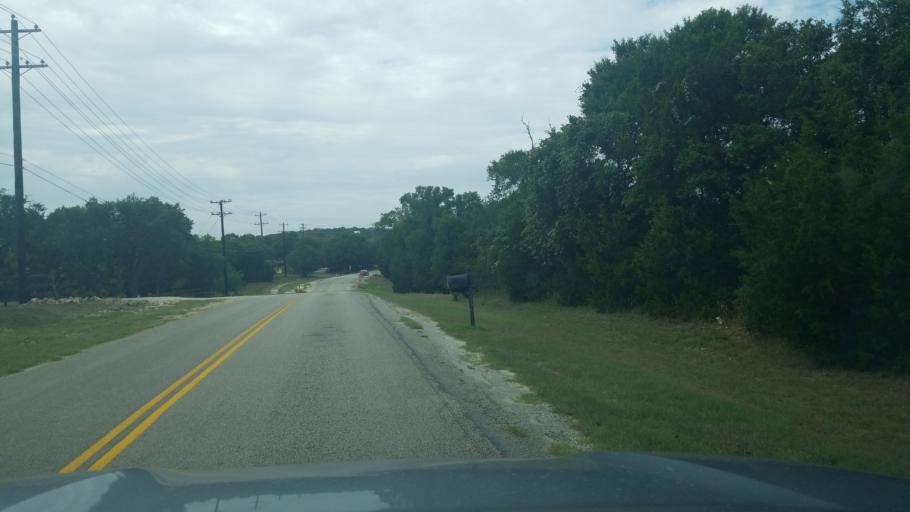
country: US
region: Texas
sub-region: Comal County
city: Bulverde
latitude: 29.7892
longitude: -98.4111
